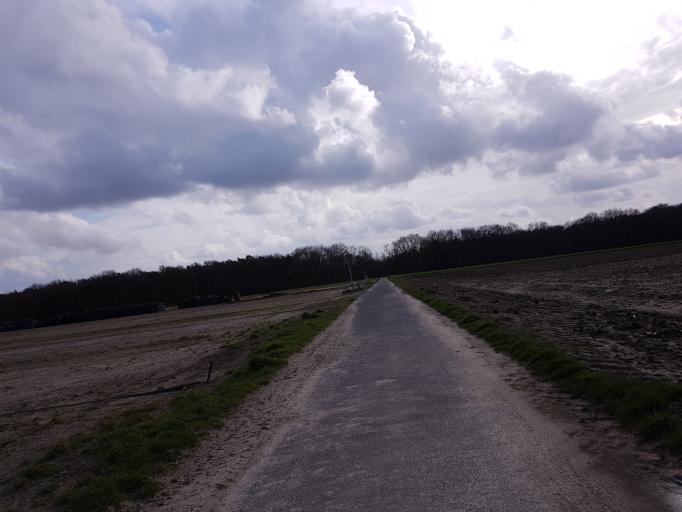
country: DE
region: North Rhine-Westphalia
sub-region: Regierungsbezirk Dusseldorf
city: Bruggen
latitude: 51.2539
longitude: 6.1932
